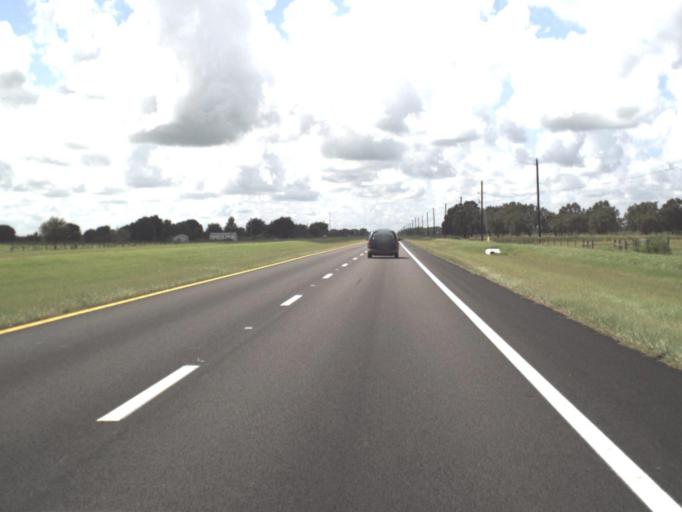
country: US
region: Florida
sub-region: Hardee County
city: Zolfo Springs
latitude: 27.4458
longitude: -81.7969
